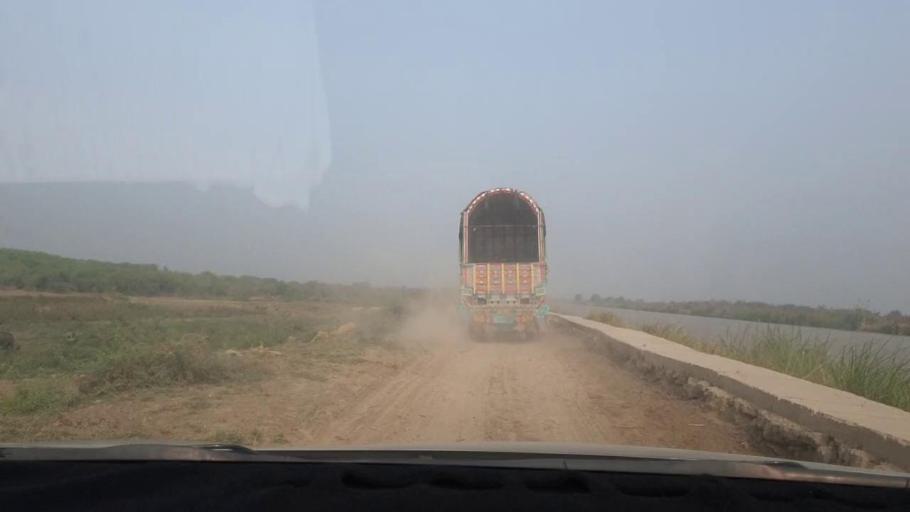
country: PK
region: Sindh
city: Matiari
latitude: 25.6567
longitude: 68.5609
